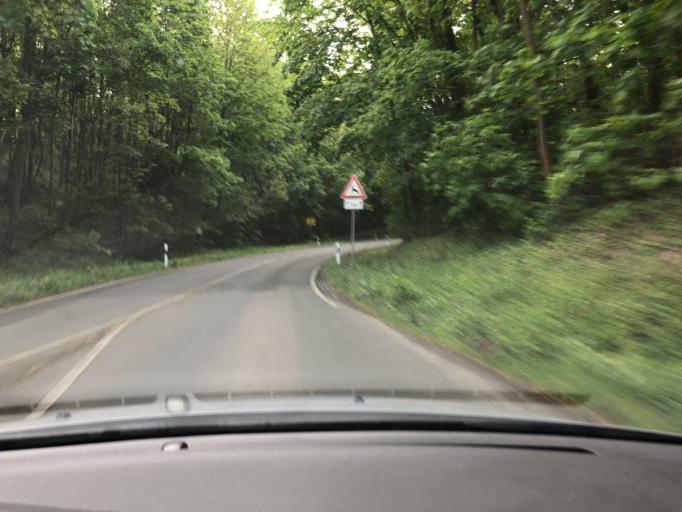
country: DE
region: Thuringia
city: Haselbach
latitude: 51.0667
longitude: 12.4374
